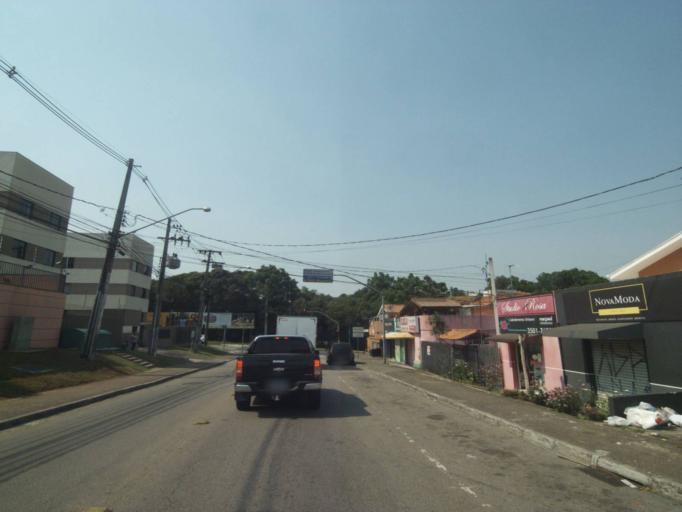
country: BR
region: Parana
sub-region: Sao Jose Dos Pinhais
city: Sao Jose dos Pinhais
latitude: -25.5240
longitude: -49.2464
